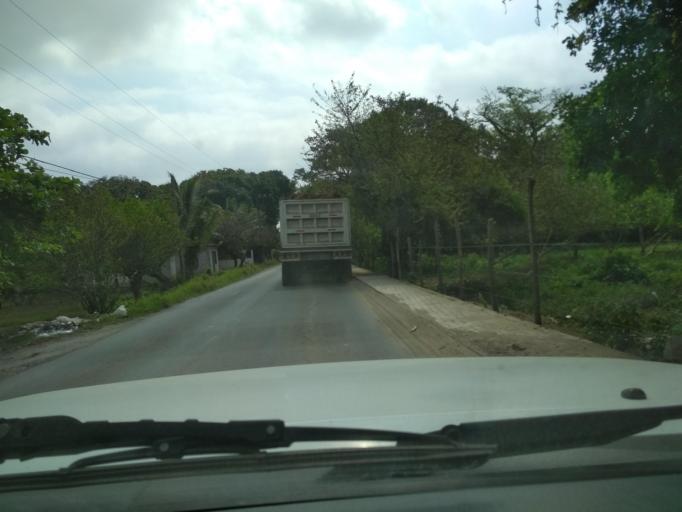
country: MX
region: Veracruz
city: El Tejar
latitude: 19.0782
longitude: -96.1735
